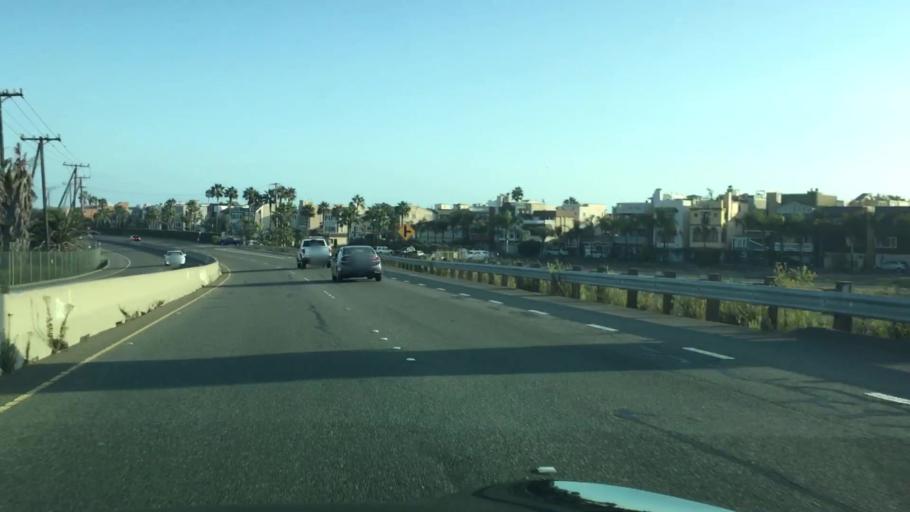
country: US
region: California
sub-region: Orange County
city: Seal Beach
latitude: 33.7305
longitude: -118.0844
